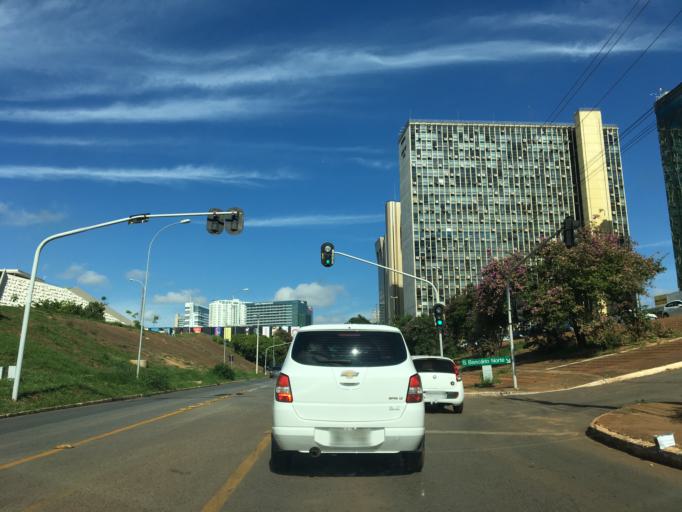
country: BR
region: Federal District
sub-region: Brasilia
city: Brasilia
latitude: -15.7920
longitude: -47.8781
